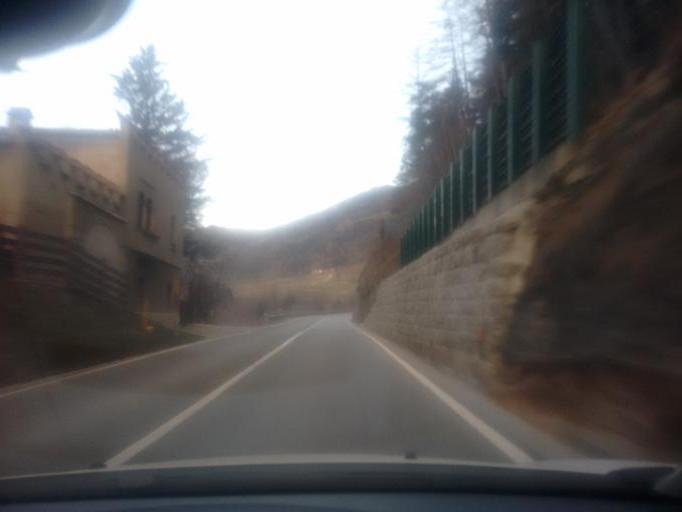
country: IT
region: Trentino-Alto Adige
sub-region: Bolzano
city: Campo di Trens
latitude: 46.8582
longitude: 11.5115
